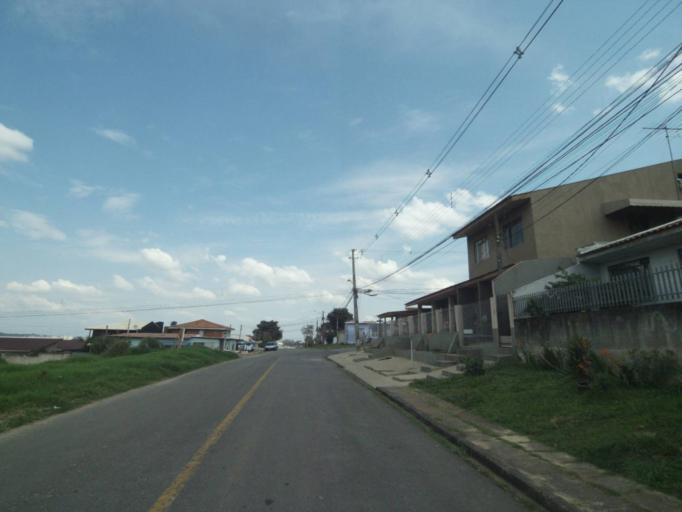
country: BR
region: Parana
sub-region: Pinhais
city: Pinhais
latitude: -25.3987
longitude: -49.1960
